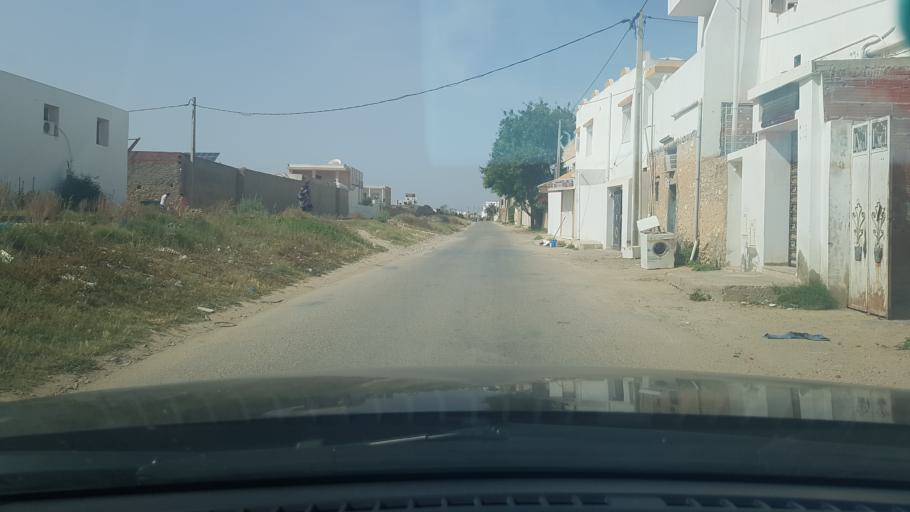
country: TN
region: Safaqis
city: Al Qarmadah
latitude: 34.8214
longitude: 10.7633
